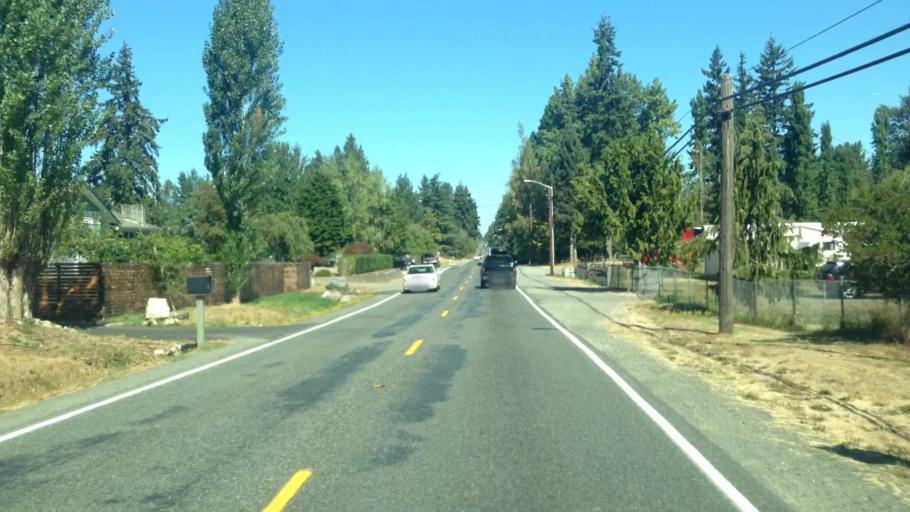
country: US
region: Washington
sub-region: Pierce County
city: Parkland
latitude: 47.1481
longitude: -122.4156
